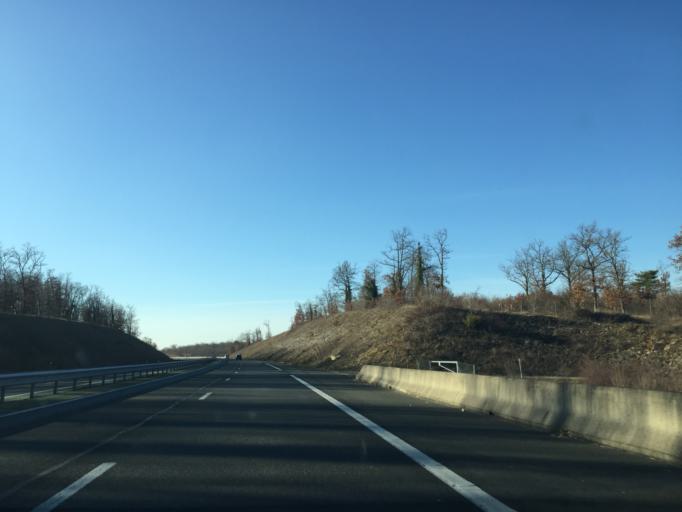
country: FR
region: Aquitaine
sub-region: Departement de la Dordogne
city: Thenon
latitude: 45.1761
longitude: 1.0128
